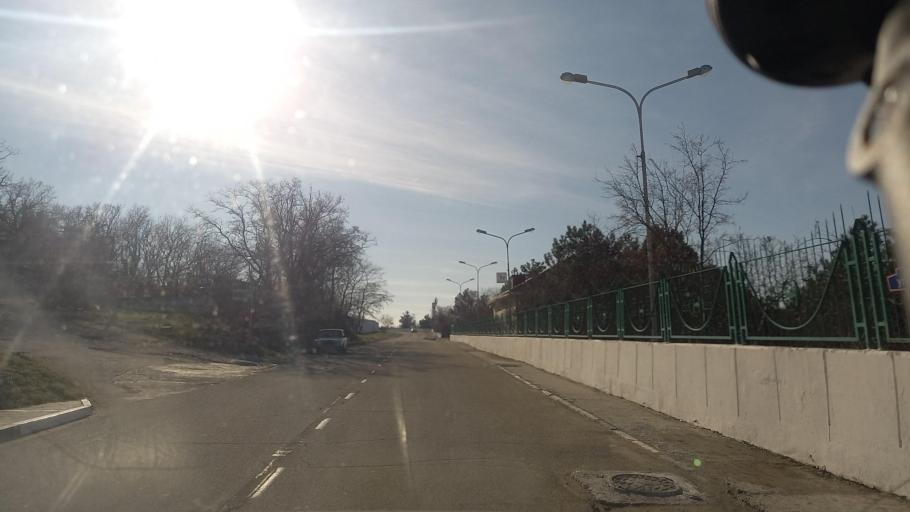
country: RU
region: Krasnodarskiy
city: Kabardinka
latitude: 44.6343
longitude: 37.9128
